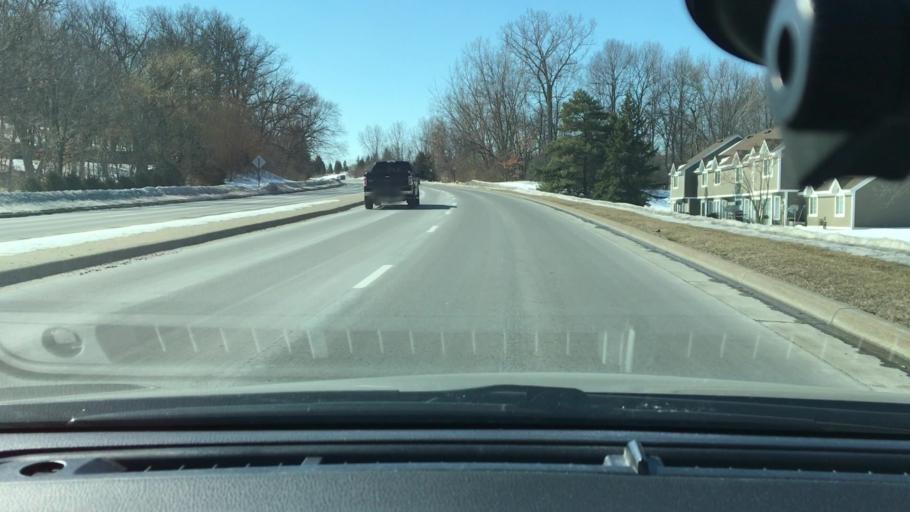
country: US
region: Minnesota
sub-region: Hennepin County
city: Maple Grove
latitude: 45.0596
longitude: -93.4441
